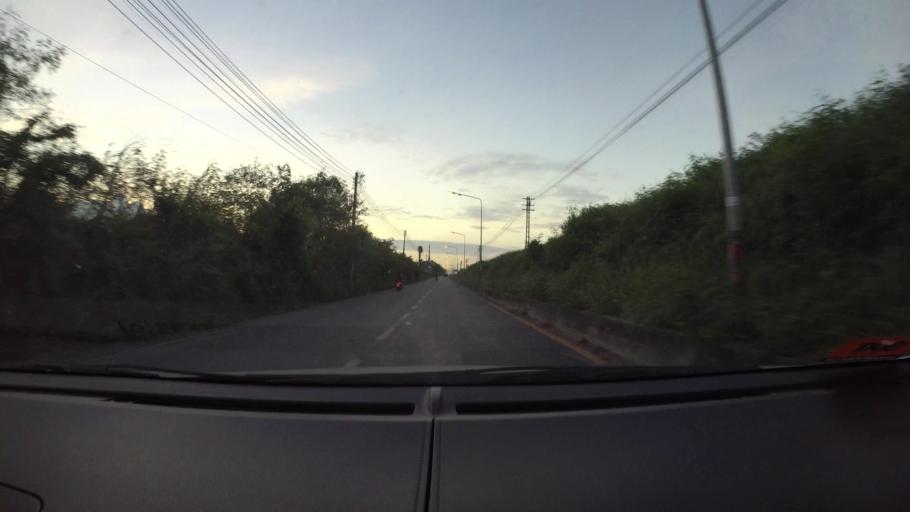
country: TH
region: Chon Buri
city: Phatthaya
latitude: 12.8709
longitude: 100.9090
